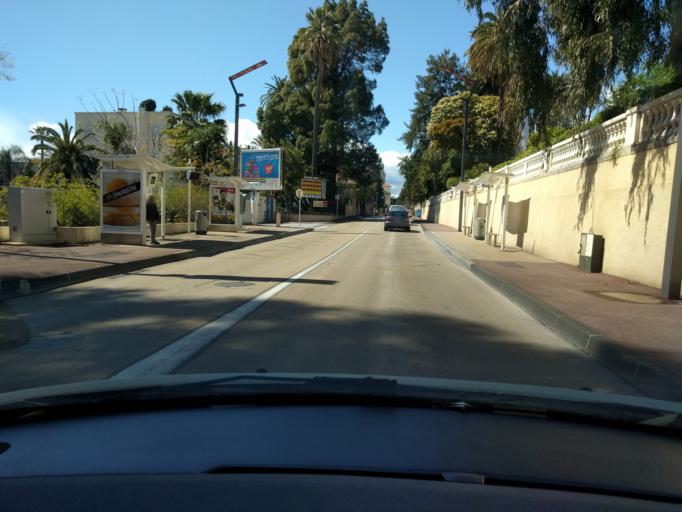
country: FR
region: Provence-Alpes-Cote d'Azur
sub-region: Departement des Alpes-Maritimes
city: Cannes
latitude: 43.5508
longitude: 7.0028
